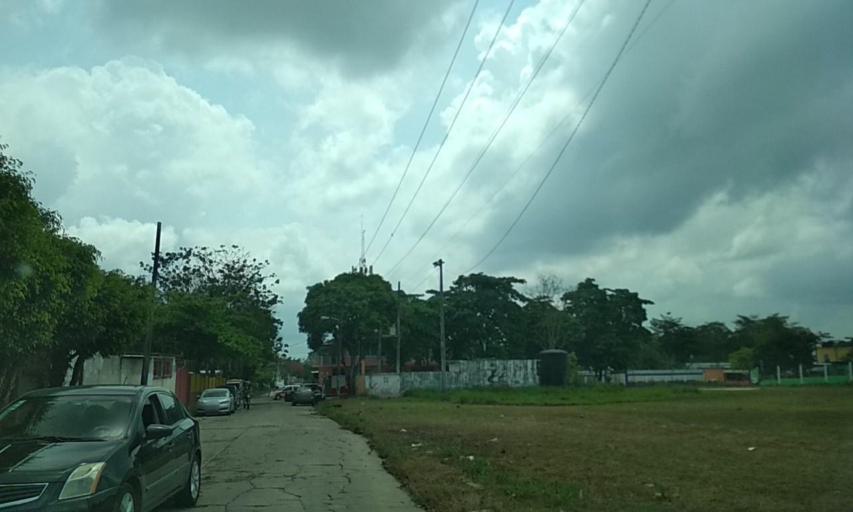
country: MX
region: Veracruz
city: Las Choapas
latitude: 17.9013
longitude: -94.1073
